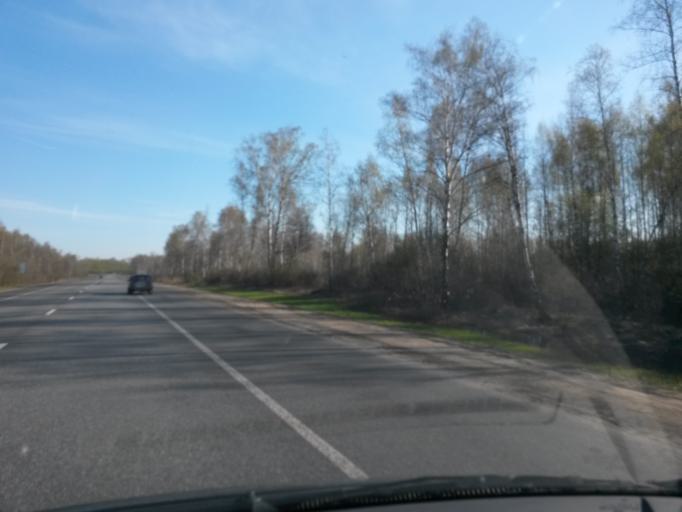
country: RU
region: Jaroslavl
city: Porech'ye-Rybnoye
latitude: 57.1157
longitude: 39.3191
